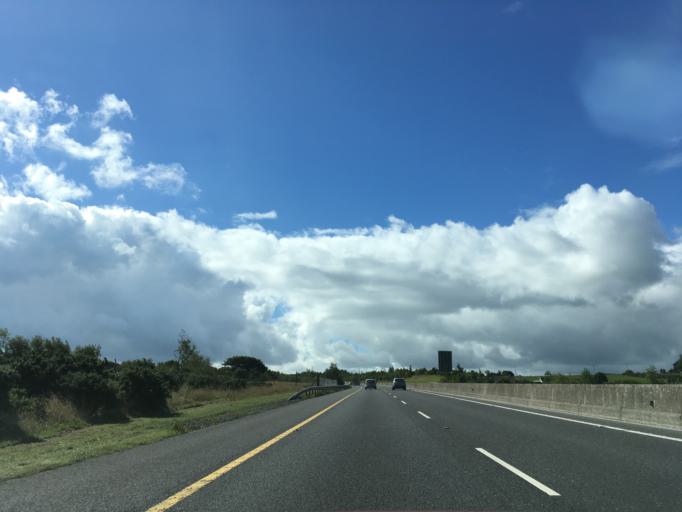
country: IE
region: Munster
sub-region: County Cork
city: Mitchelstown
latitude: 52.2270
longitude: -8.2873
